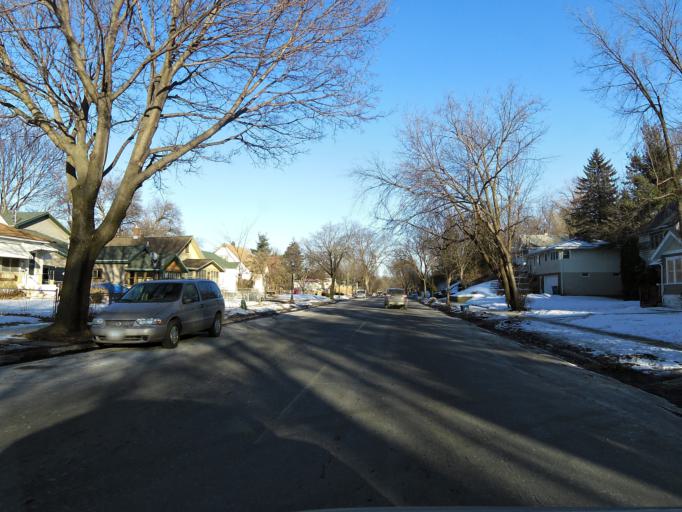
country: US
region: Minnesota
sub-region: Ramsey County
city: Maplewood
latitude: 44.9630
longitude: -93.0244
